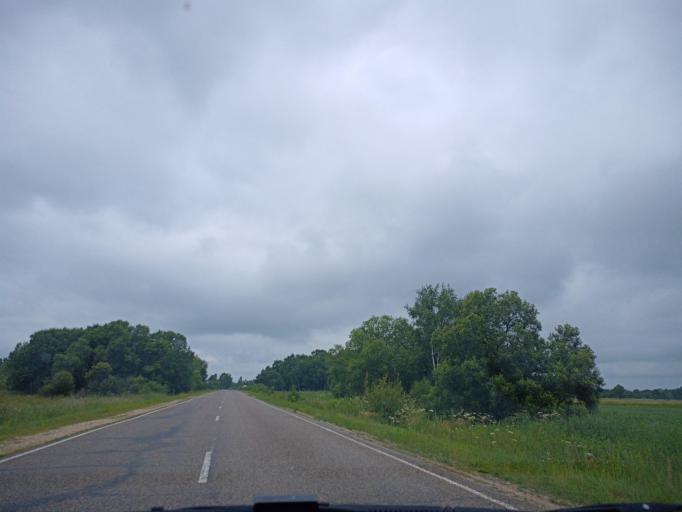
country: RU
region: Primorskiy
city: Novopokrovka
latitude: 45.9646
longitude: 134.2604
